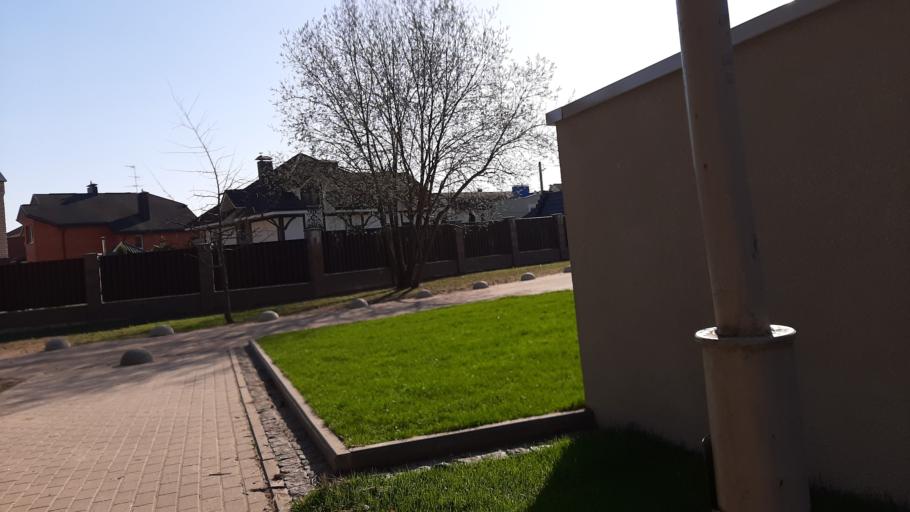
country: BY
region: Minsk
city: Bal'shavik
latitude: 53.9576
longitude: 27.5901
